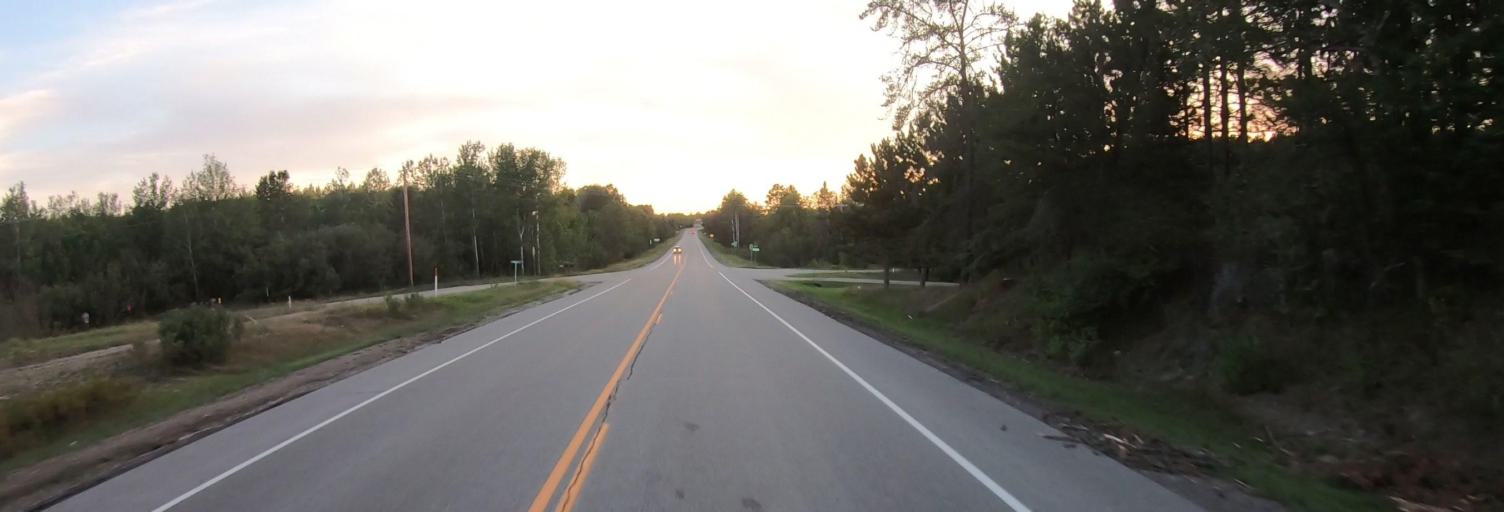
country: US
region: Minnesota
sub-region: Saint Louis County
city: Aurora
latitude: 47.8070
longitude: -92.2615
